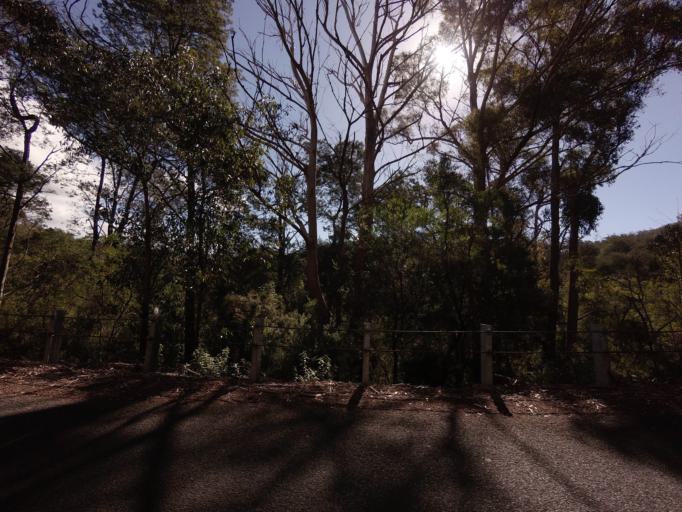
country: AU
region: Tasmania
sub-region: Break O'Day
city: St Helens
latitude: -41.6371
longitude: 148.2429
